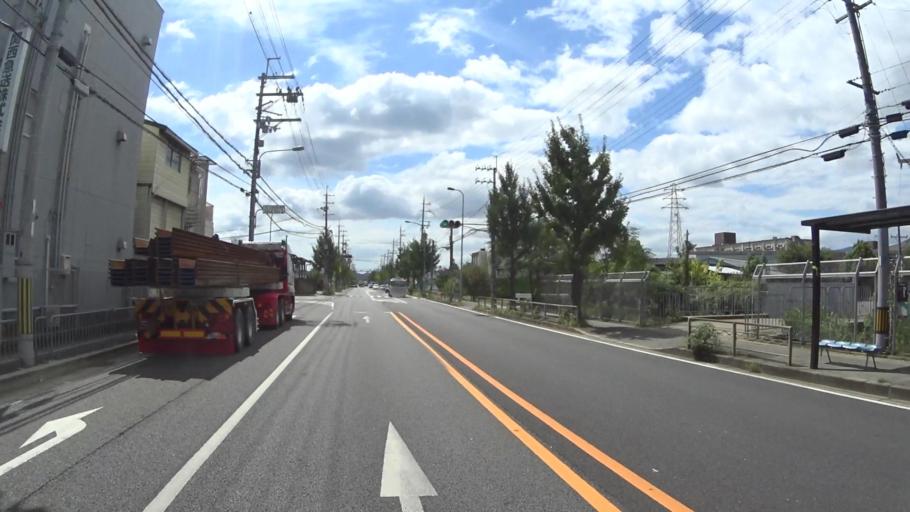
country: JP
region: Kyoto
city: Muko
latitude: 34.9208
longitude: 135.7325
